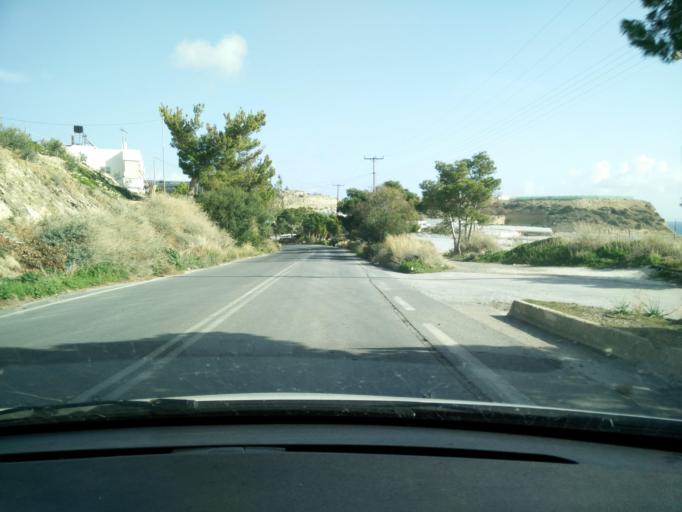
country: GR
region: Crete
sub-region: Nomos Lasithiou
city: Gra Liyia
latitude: 35.0086
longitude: 25.6296
